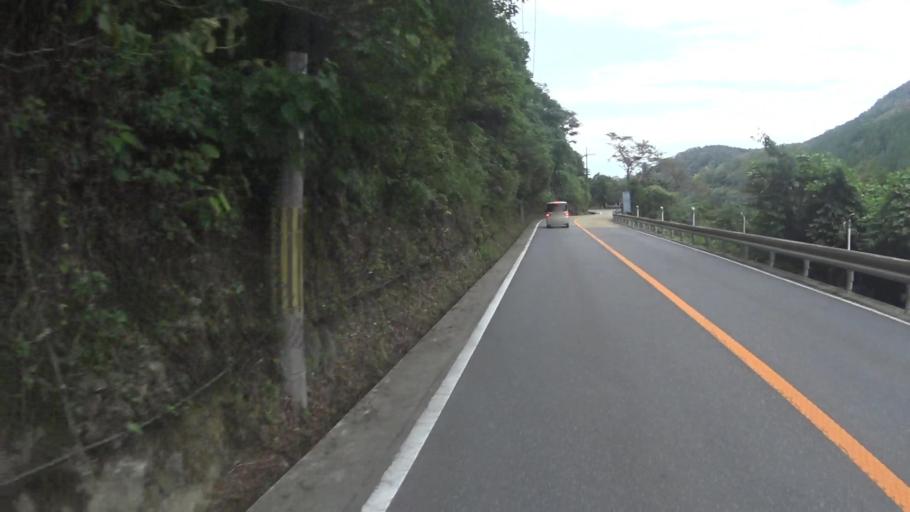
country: JP
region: Kyoto
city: Uji
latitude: 34.8737
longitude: 135.8311
